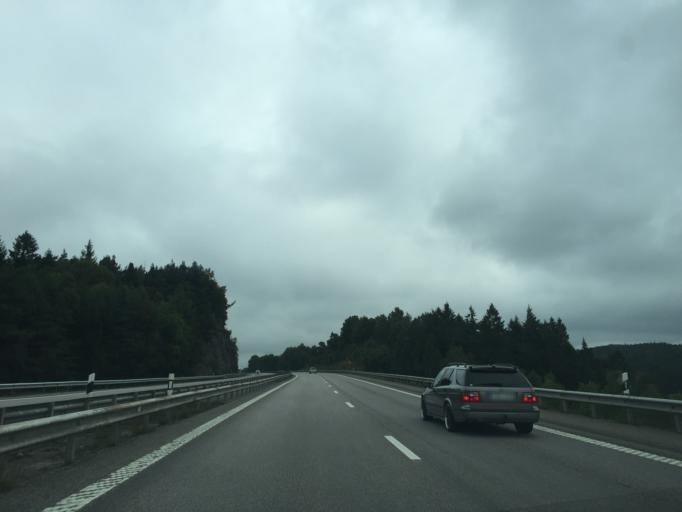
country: SE
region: Halland
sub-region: Kungsbacka Kommun
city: Fjaeras kyrkby
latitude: 57.3921
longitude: 12.1889
